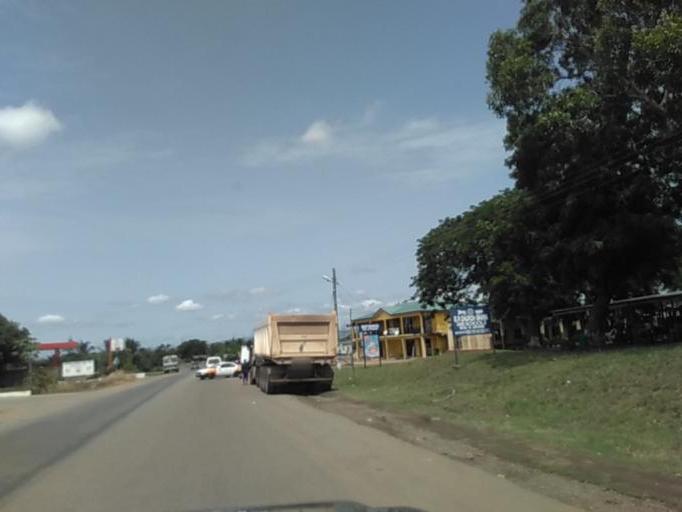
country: GH
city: Akropong
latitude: 6.1524
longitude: 0.0590
